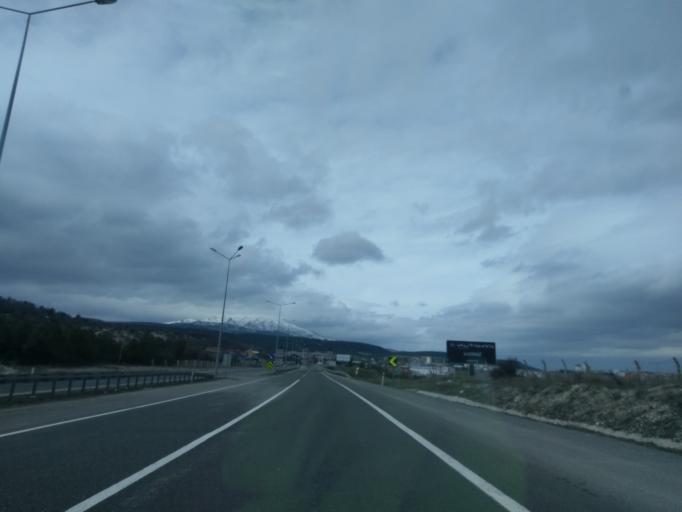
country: TR
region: Kuetahya
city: Kutahya
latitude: 39.3756
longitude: 30.0612
